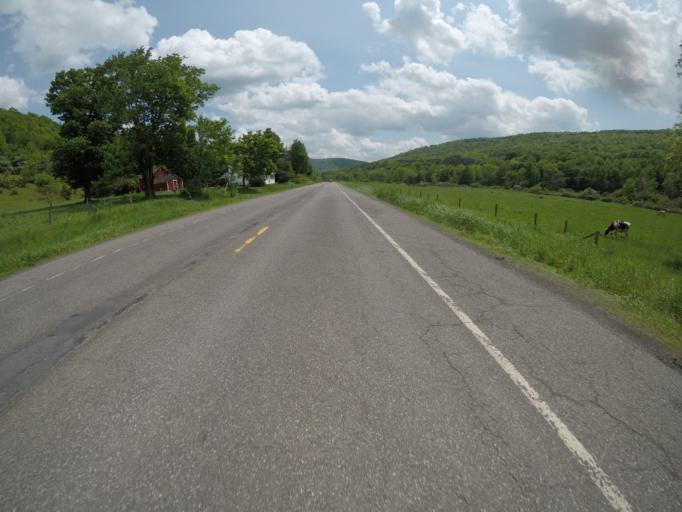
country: US
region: New York
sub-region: Delaware County
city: Stamford
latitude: 42.2355
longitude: -74.5987
